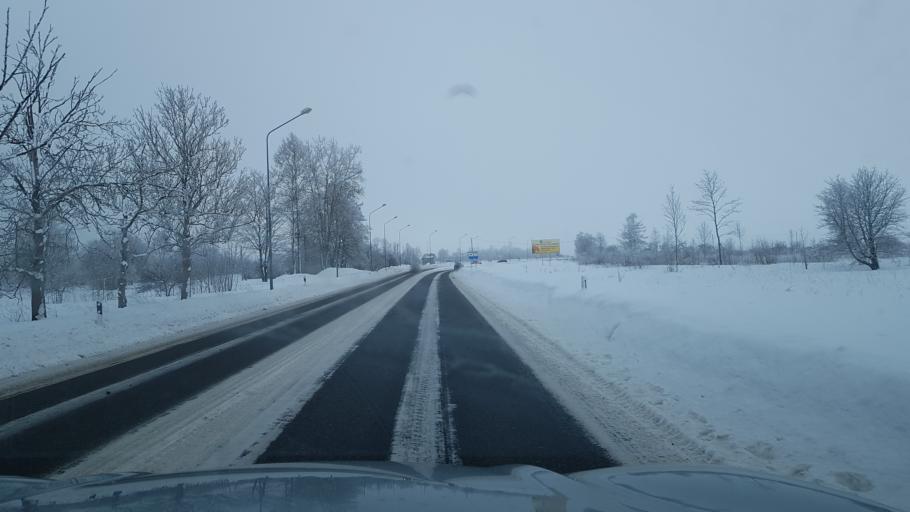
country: EE
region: Ida-Virumaa
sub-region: Johvi vald
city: Johvi
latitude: 59.3323
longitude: 27.4029
